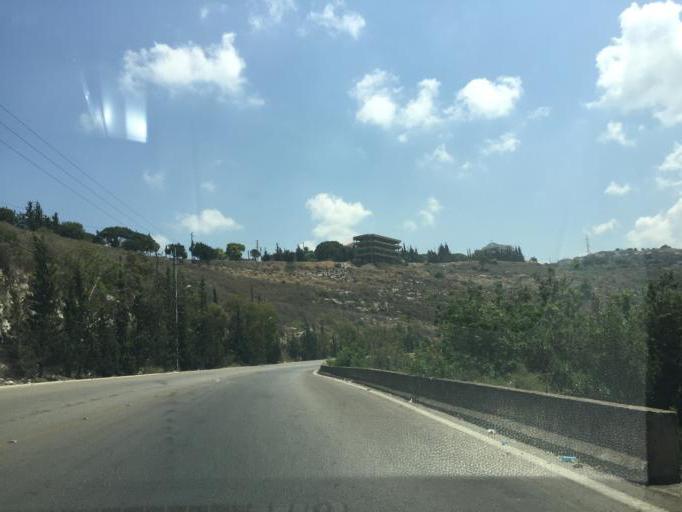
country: LB
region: Mont-Liban
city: Beit ed Dine
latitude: 33.7084
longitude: 35.4535
